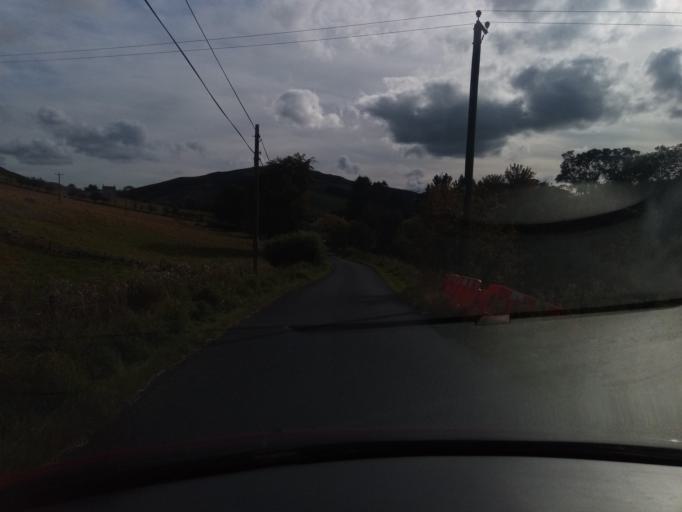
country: GB
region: Scotland
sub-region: The Scottish Borders
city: Kelso
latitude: 55.4700
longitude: -2.3530
